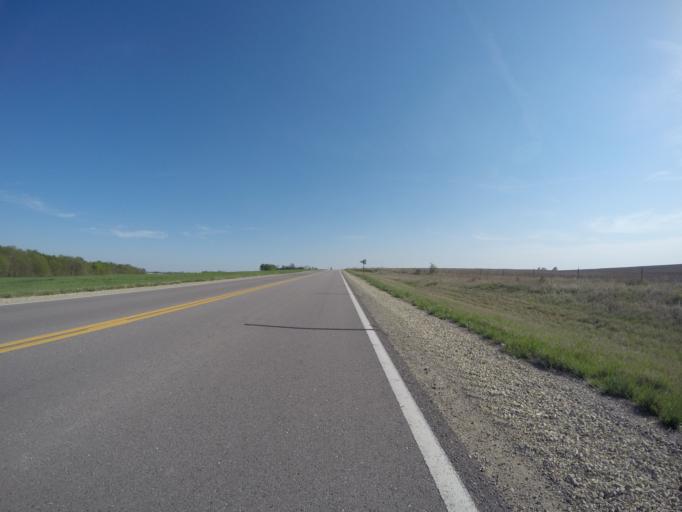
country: US
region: Kansas
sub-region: Riley County
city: Fort Riley North
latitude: 39.2958
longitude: -96.7750
